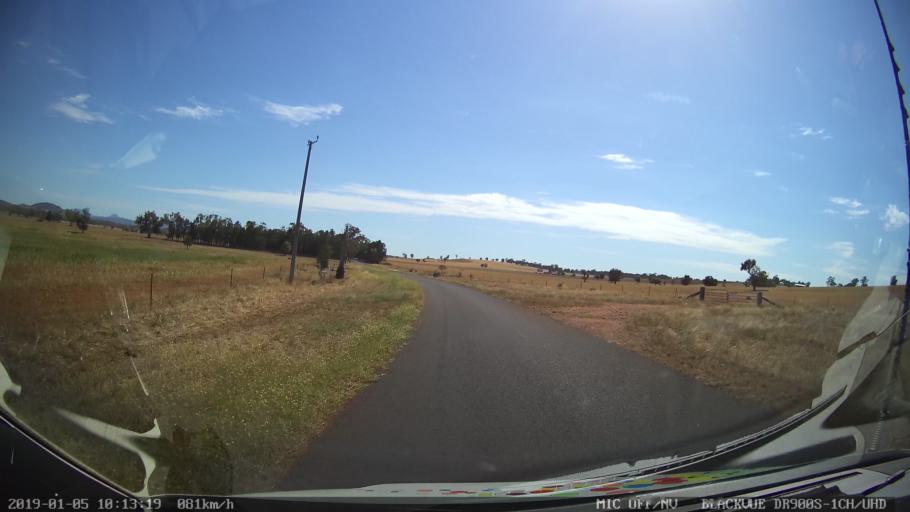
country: AU
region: New South Wales
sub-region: Gilgandra
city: Gilgandra
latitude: -31.6031
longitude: 148.9235
